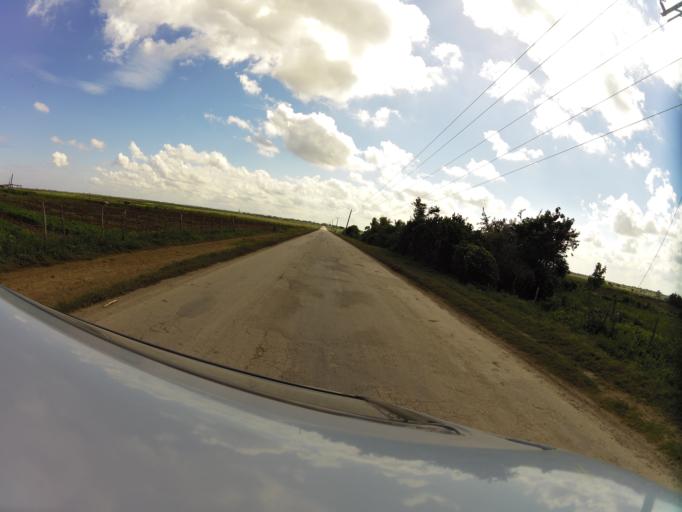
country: CU
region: Las Tunas
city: Jesus Menendez
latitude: 21.2193
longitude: -76.4190
